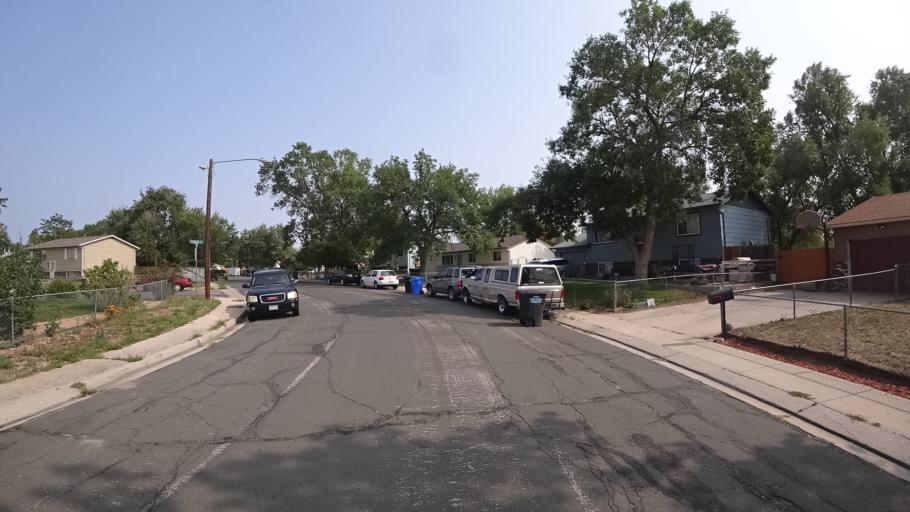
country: US
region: Colorado
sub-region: El Paso County
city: Stratmoor
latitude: 38.7956
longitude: -104.7635
